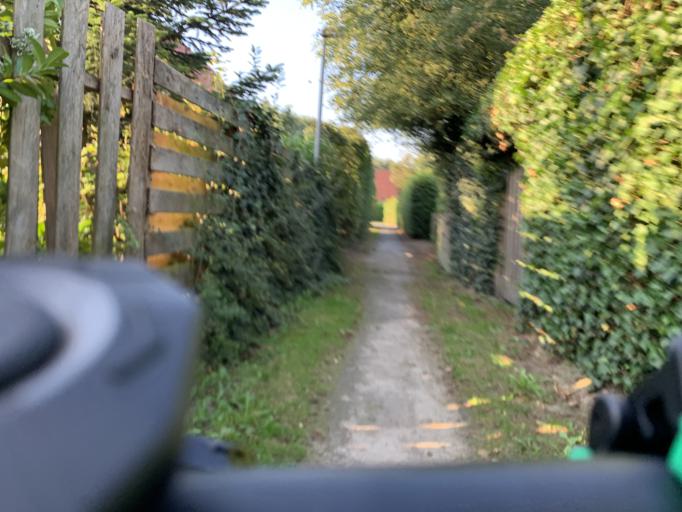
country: DE
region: Lower Saxony
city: Westerstede
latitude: 53.2535
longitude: 7.8991
